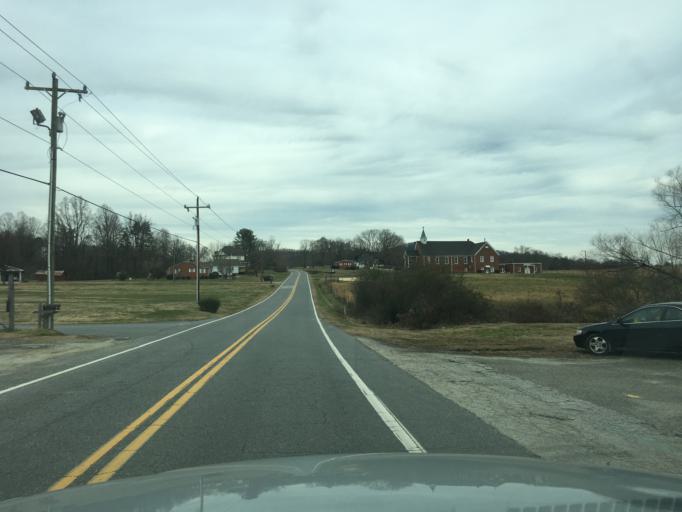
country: US
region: North Carolina
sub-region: McDowell County
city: West Marion
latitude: 35.6154
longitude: -81.9818
